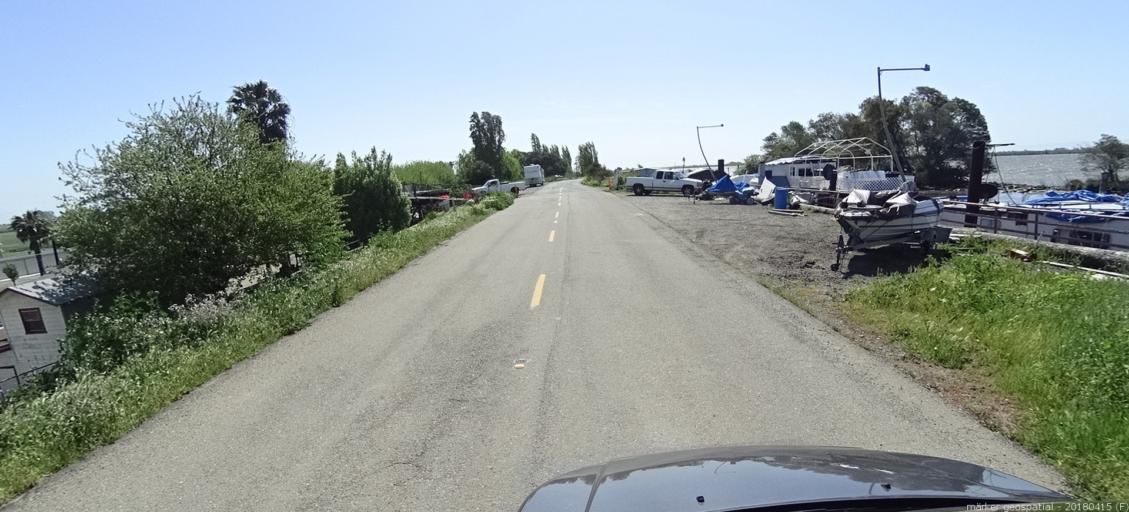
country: US
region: California
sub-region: Contra Costa County
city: Bethel Island
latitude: 38.1052
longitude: -121.5940
